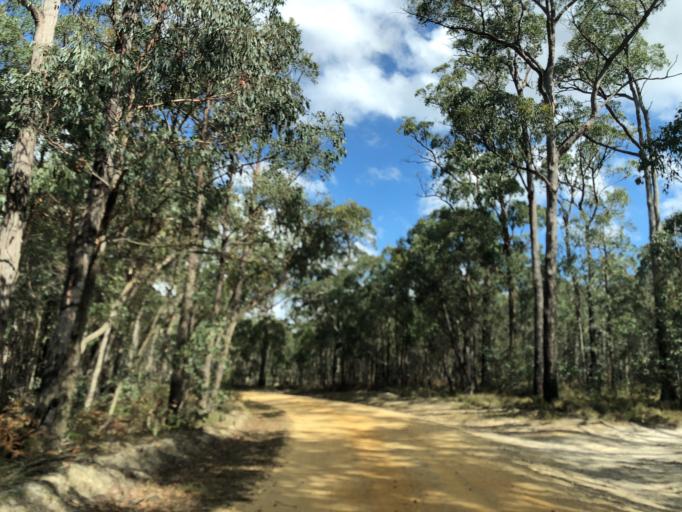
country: AU
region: Victoria
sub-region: Moorabool
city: Bacchus Marsh
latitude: -37.5247
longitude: 144.3224
